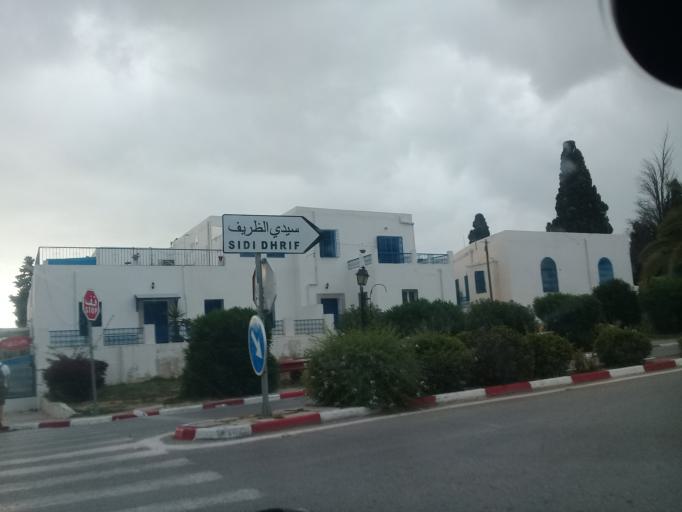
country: TN
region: Tunis
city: Sidi Bou Said
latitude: 36.8703
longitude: 10.3435
